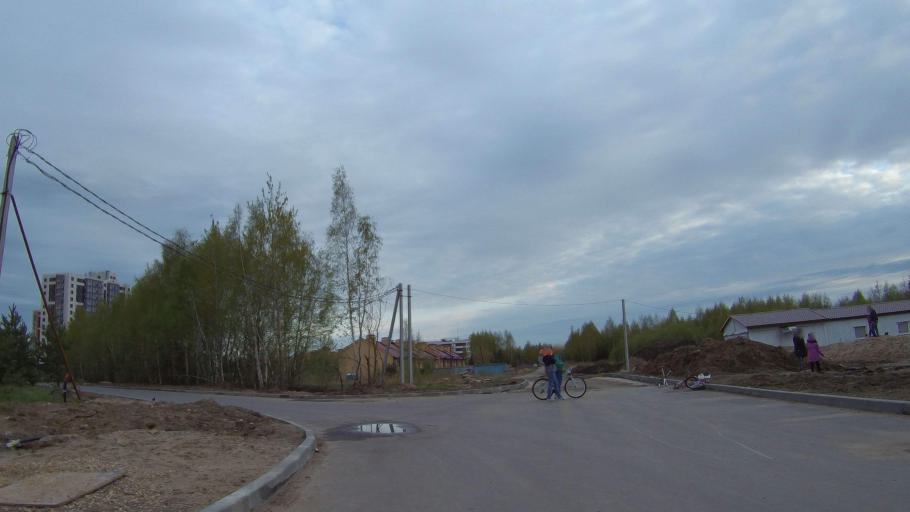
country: RU
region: Moskovskaya
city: Ramenskoye
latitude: 55.5933
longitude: 38.2475
